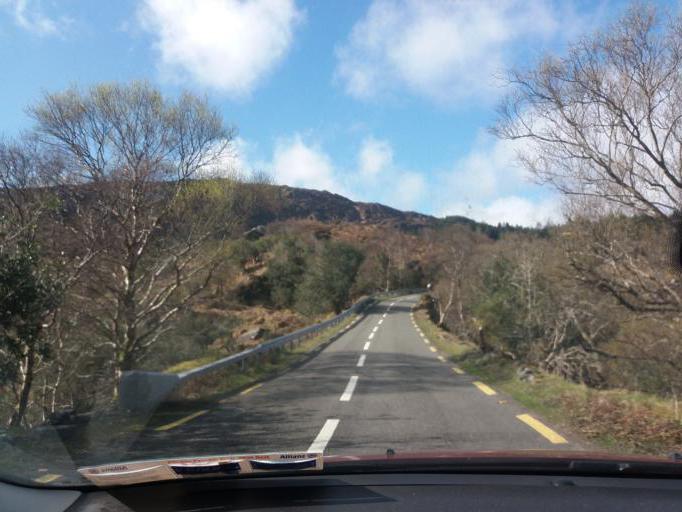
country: IE
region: Munster
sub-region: Ciarrai
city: Kenmare
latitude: 51.9660
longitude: -9.5978
